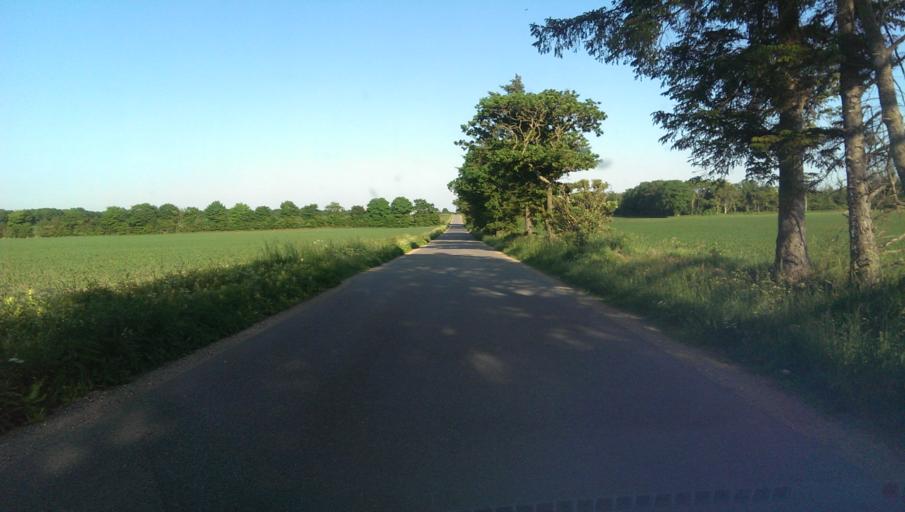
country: DK
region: South Denmark
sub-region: Esbjerg Kommune
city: Bramming
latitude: 55.5507
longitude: 8.6388
